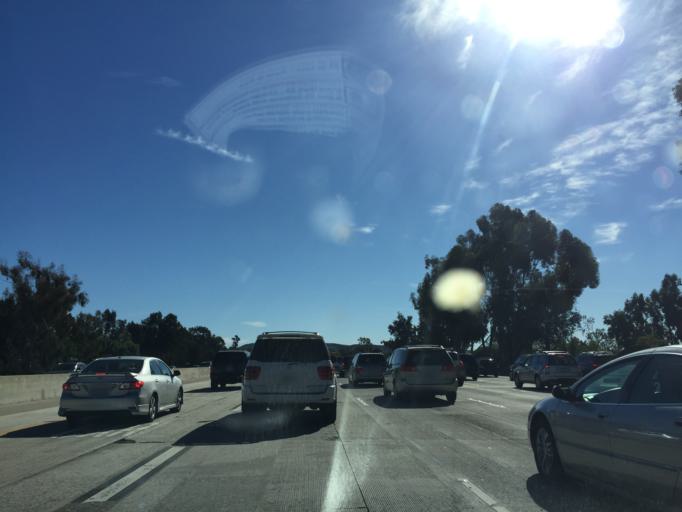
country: US
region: California
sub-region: Orange County
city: San Juan Capistrano
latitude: 33.5203
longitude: -117.6657
